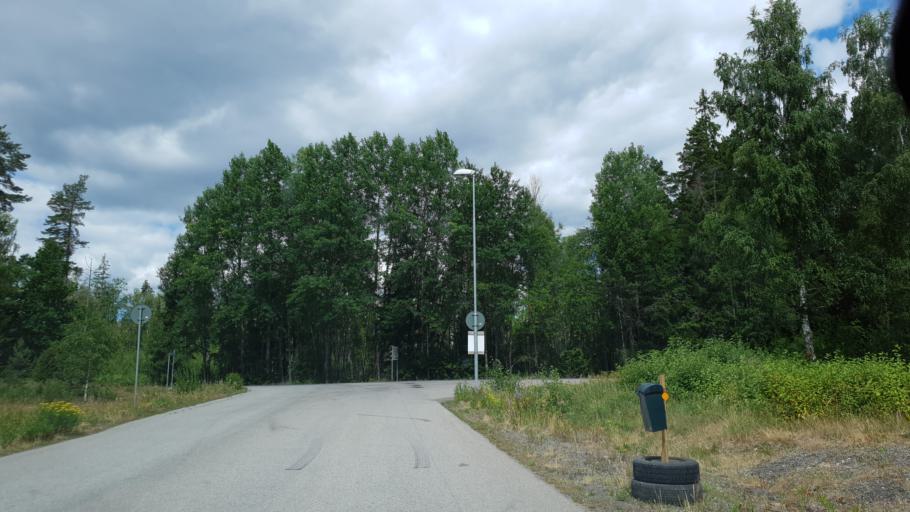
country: SE
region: Kronoberg
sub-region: Uppvidinge Kommun
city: Aseda
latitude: 57.1715
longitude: 15.3685
